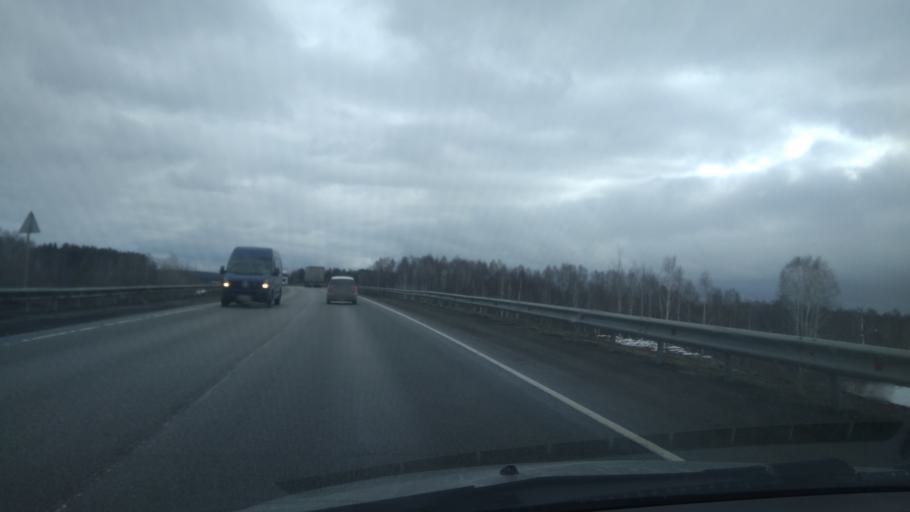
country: RU
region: Sverdlovsk
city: Ufimskiy
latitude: 56.7649
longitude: 58.1384
